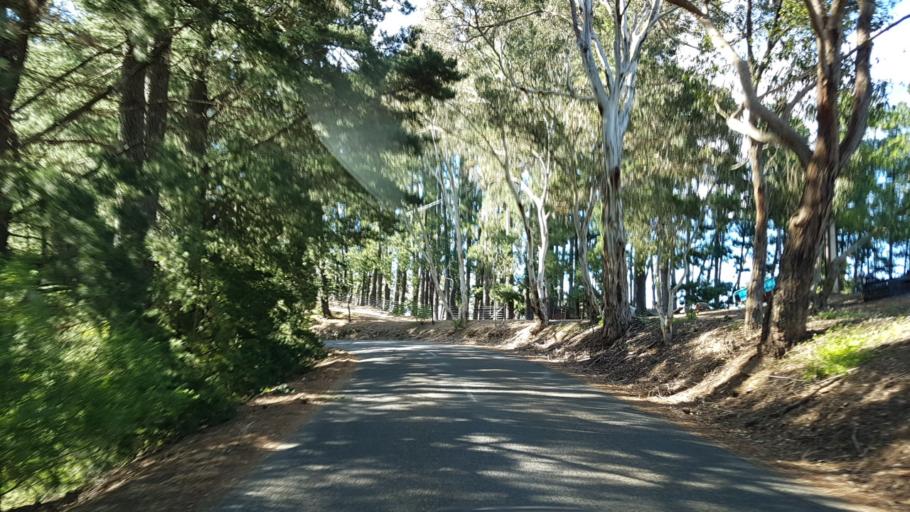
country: AU
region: South Australia
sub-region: Adelaide Hills
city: Adelaide Hills
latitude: -34.9103
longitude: 138.7624
